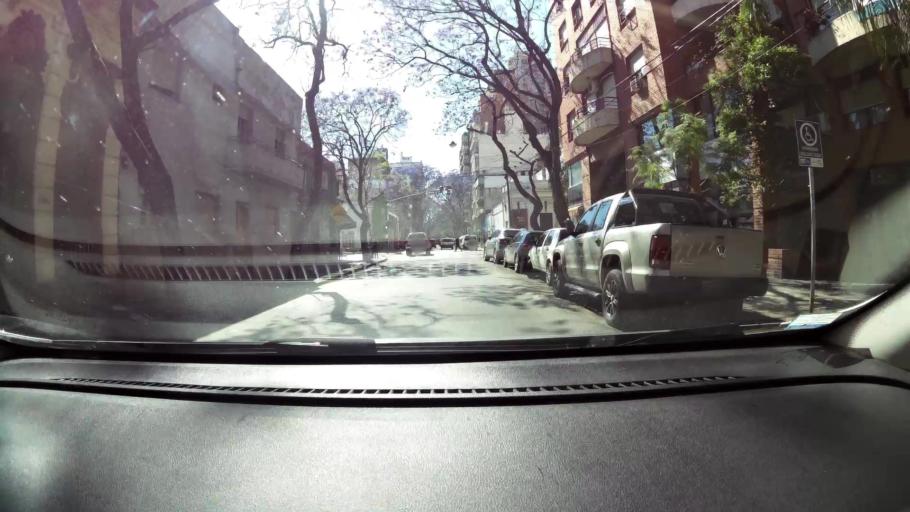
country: AR
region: Santa Fe
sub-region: Departamento de Rosario
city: Rosario
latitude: -32.9543
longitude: -60.6376
